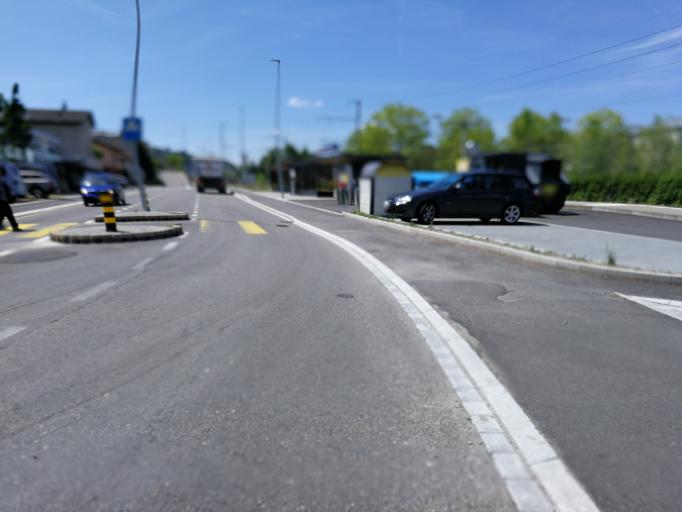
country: CH
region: Schwyz
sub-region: Bezirk Hoefe
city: Feusisberg
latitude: 47.1976
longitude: 8.7350
